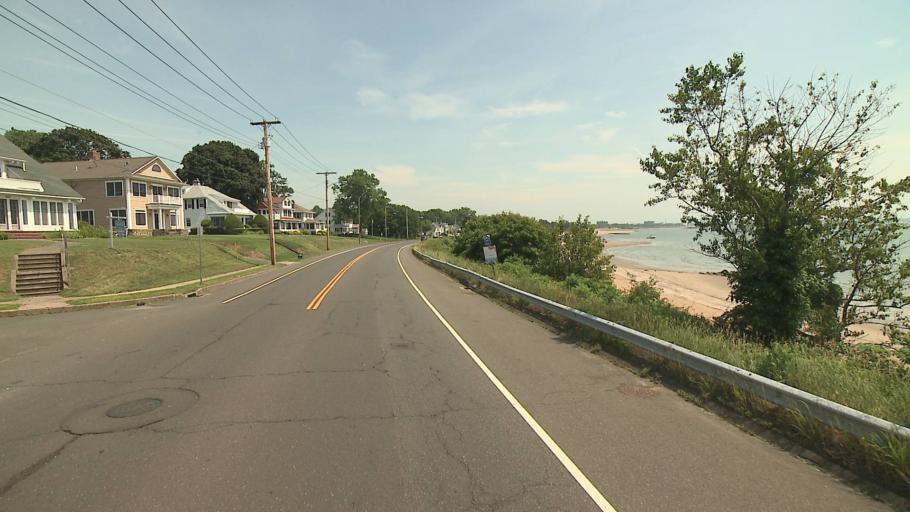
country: US
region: Connecticut
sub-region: New Haven County
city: Woodmont
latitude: 41.2419
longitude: -72.9708
